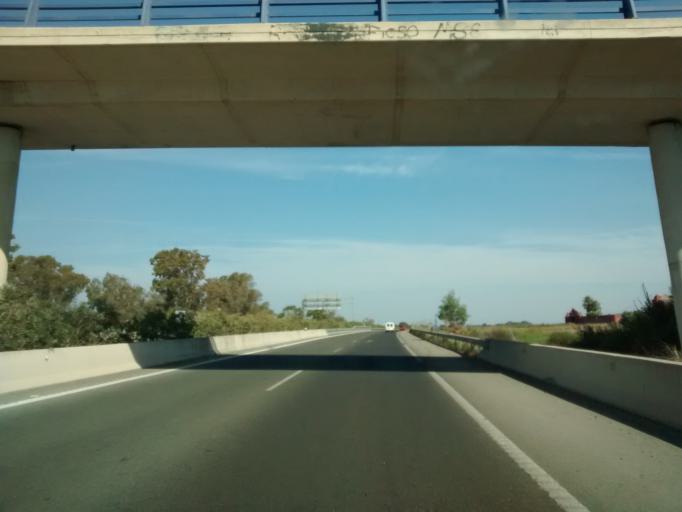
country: ES
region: Andalusia
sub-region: Provincia de Cadiz
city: Chiclana de la Frontera
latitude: 36.3610
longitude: -6.1096
